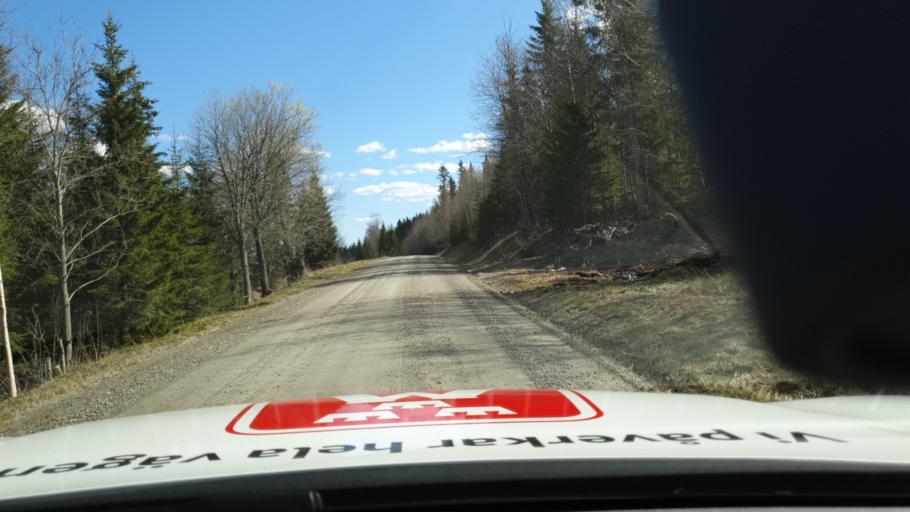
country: SE
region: Jaemtland
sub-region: Bergs Kommun
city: Hoverberg
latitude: 62.9271
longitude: 14.2962
